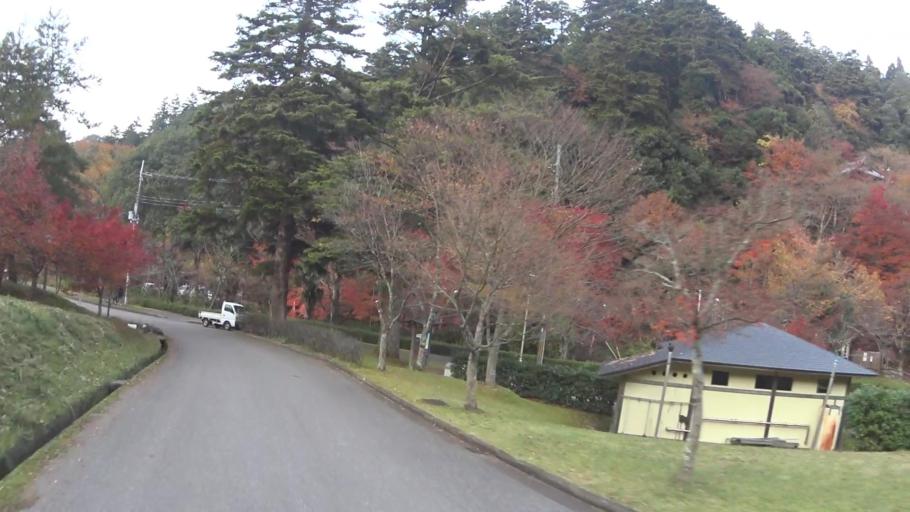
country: JP
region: Kyoto
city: Maizuru
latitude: 35.4752
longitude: 135.4476
